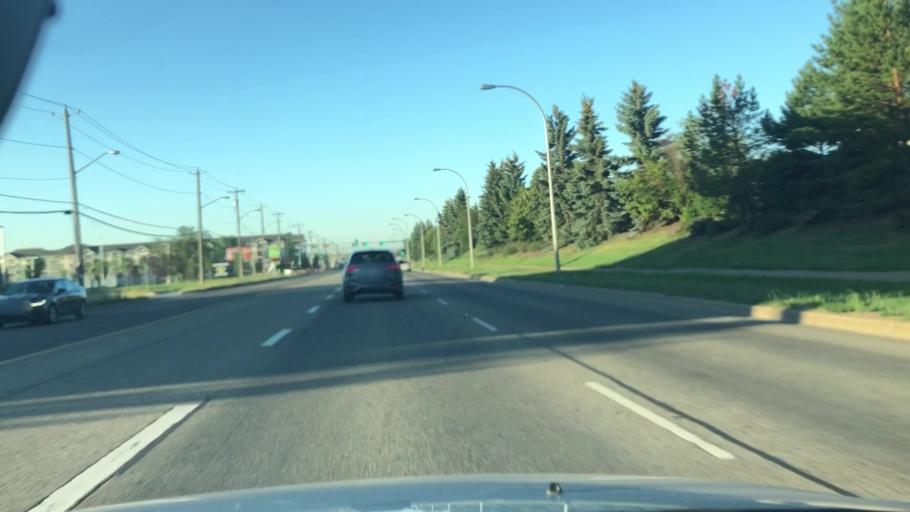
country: CA
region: Alberta
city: Edmonton
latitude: 53.6085
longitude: -113.5413
